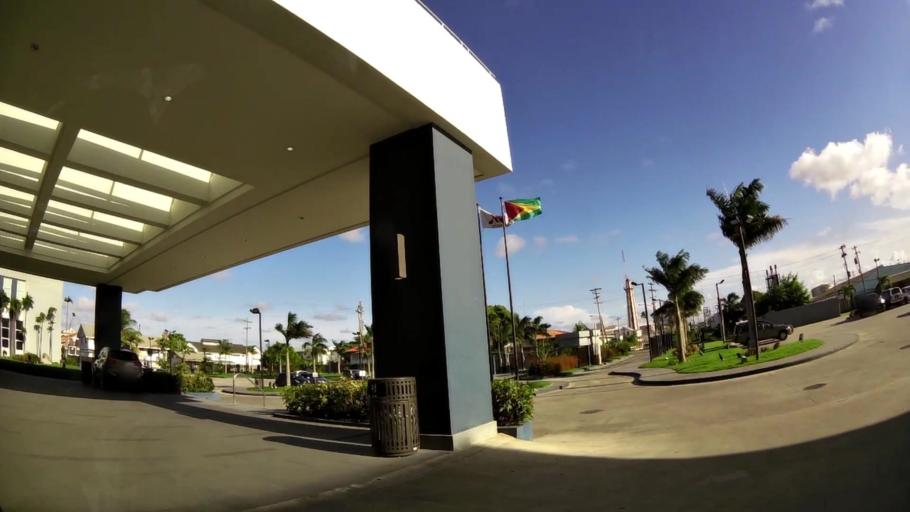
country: GY
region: Demerara-Mahaica
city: Georgetown
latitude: 6.8256
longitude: -58.1639
